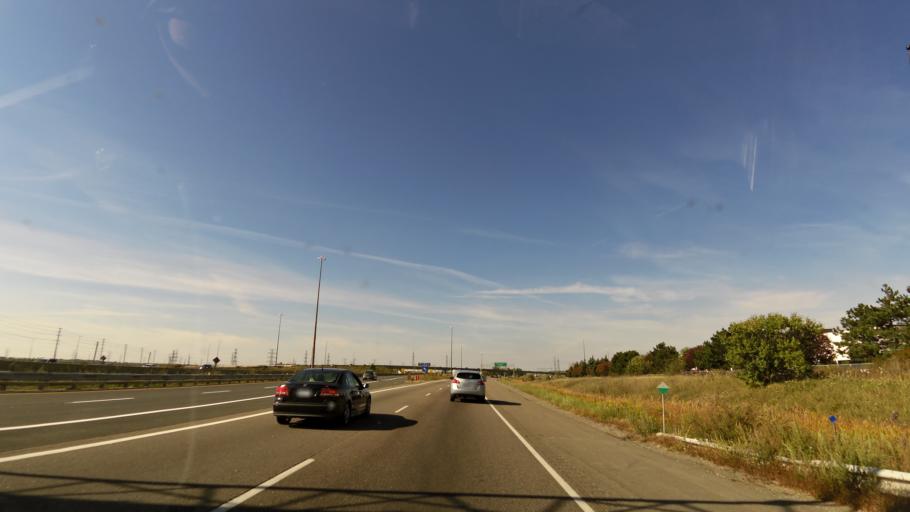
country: CA
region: Ontario
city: Mississauga
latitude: 43.5243
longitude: -79.7179
